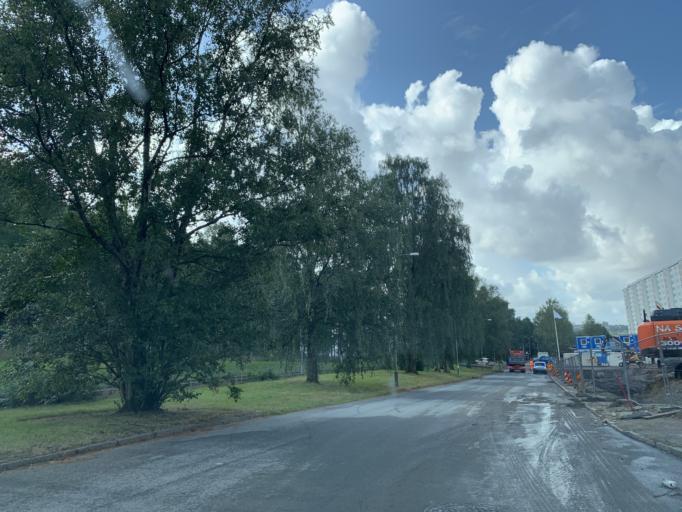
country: SE
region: Vaestra Goetaland
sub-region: Goteborg
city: Eriksbo
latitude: 57.7417
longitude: 12.0294
